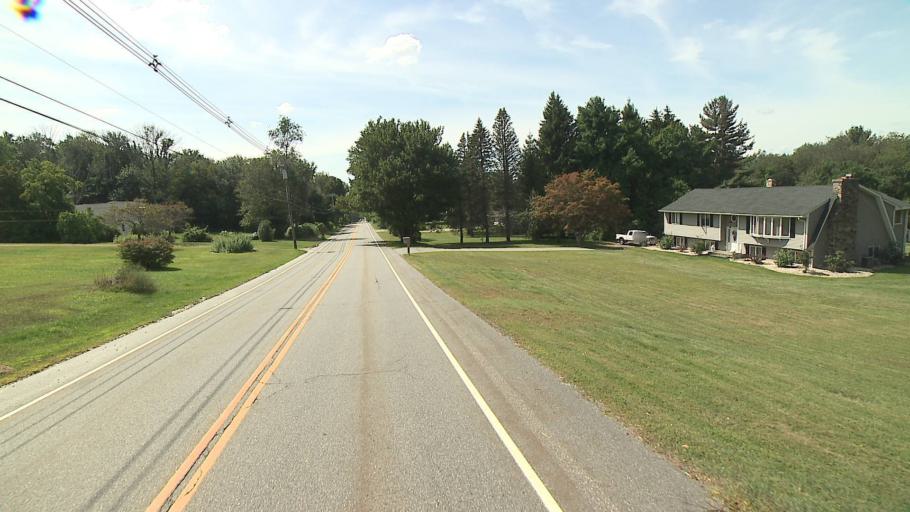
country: US
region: Connecticut
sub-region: Litchfield County
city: Bethlehem Village
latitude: 41.6527
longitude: -73.2019
